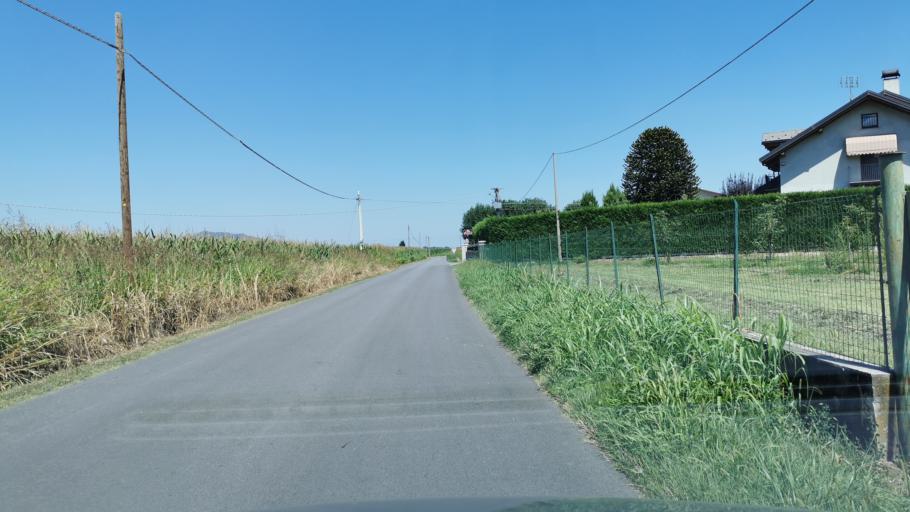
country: IT
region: Piedmont
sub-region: Provincia di Cuneo
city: Caraglio
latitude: 44.4258
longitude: 7.4341
